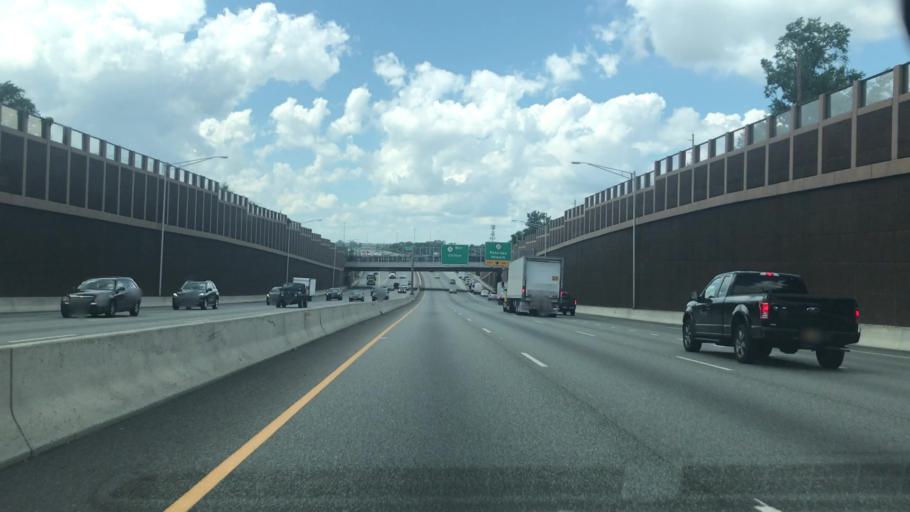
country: US
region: New Jersey
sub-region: Bergen County
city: Lyndhurst
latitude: 40.8184
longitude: -74.1199
